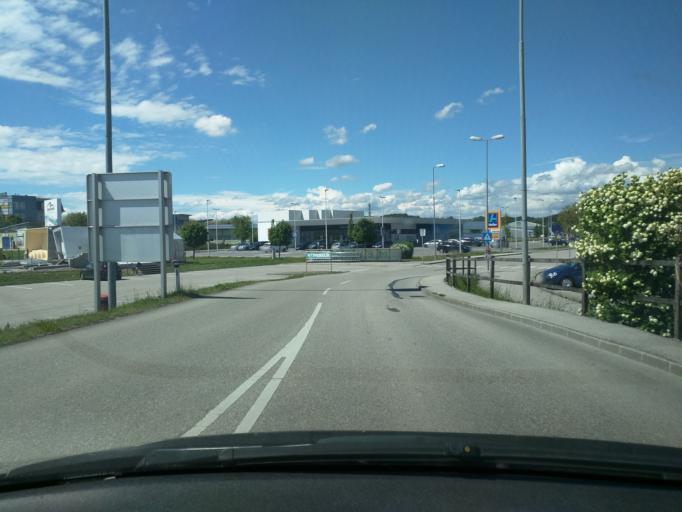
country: AT
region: Lower Austria
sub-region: Politischer Bezirk Amstetten
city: Amstetten
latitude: 48.1162
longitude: 14.9113
